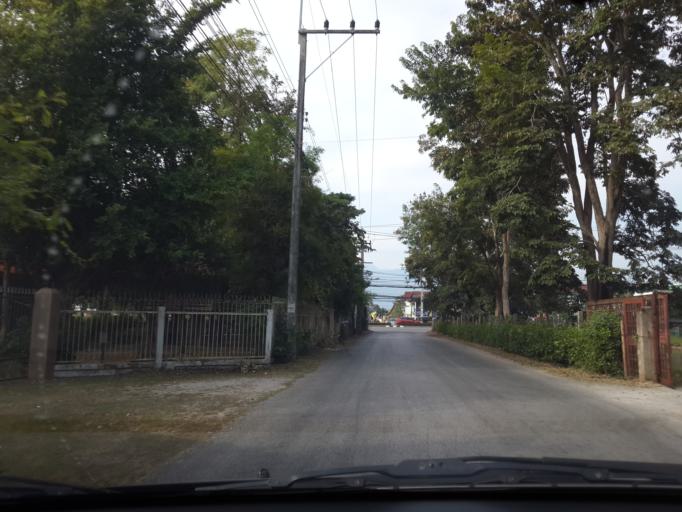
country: TH
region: Chiang Mai
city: San Sai
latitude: 18.9011
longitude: 99.0069
